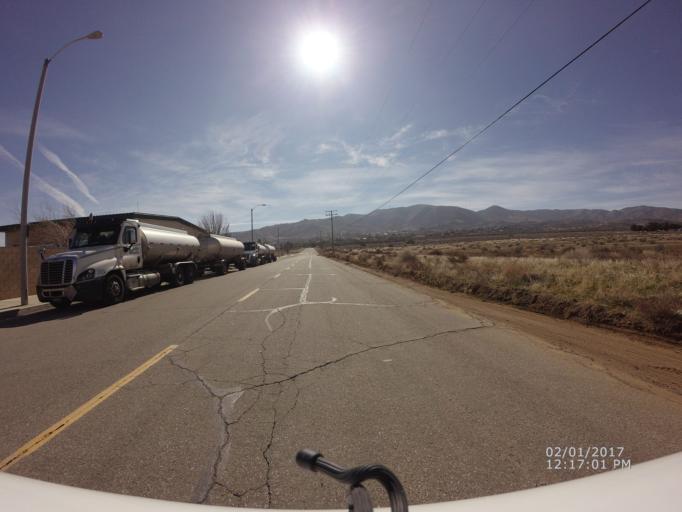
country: US
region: California
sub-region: Los Angeles County
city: Palmdale
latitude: 34.5567
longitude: -118.1357
